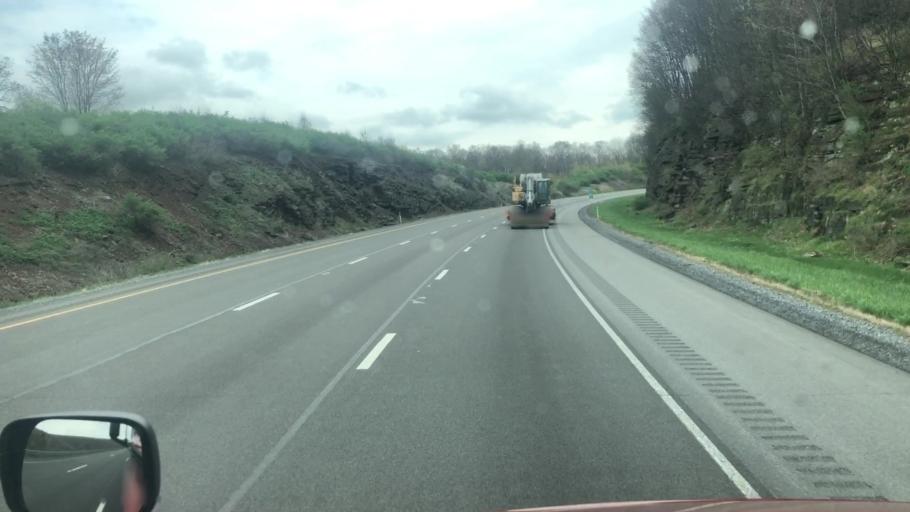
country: US
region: Pennsylvania
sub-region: Clinton County
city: Castanea
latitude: 41.0616
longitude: -77.3687
